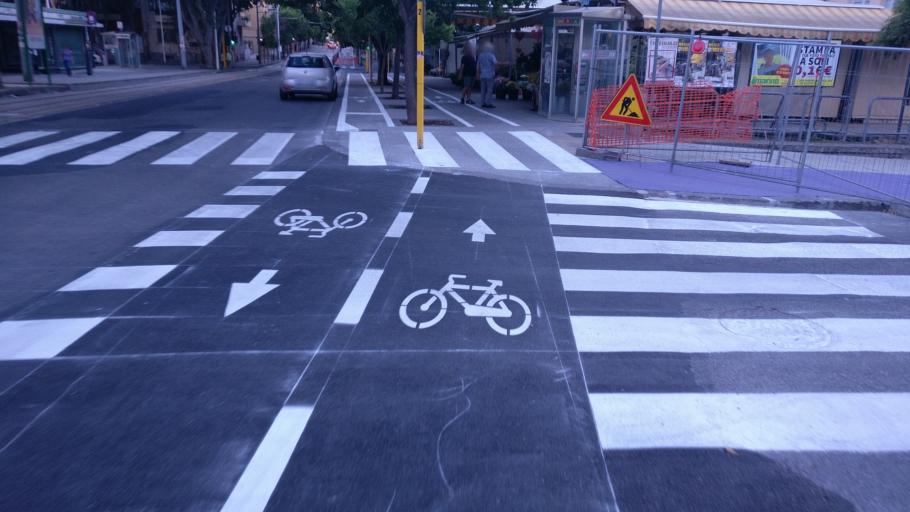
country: IT
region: Sardinia
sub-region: Provincia di Sassari
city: Sassari
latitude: 40.7209
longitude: 8.5582
